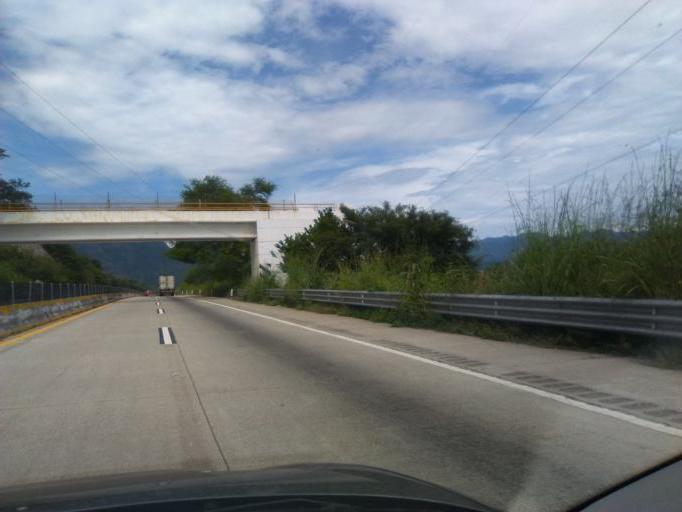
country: MX
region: Guerrero
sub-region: Chilpancingo de los Bravo
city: Mohoneras
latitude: 17.2344
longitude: -99.5244
